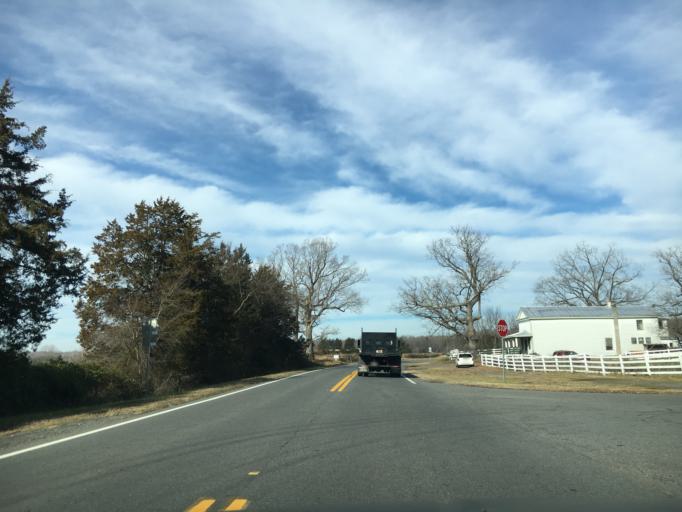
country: US
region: Virginia
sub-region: Louisa County
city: Louisa
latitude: 38.1590
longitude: -77.9303
